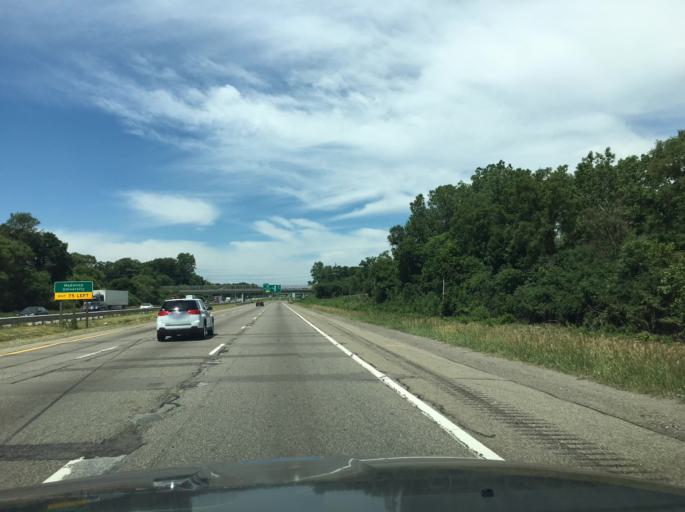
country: US
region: Michigan
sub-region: Oakland County
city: Bloomfield Hills
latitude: 42.6097
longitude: -83.2195
